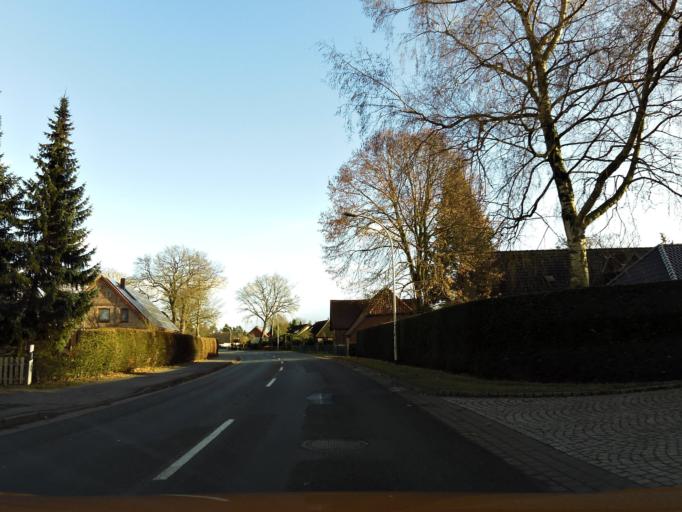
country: DE
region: Lower Saxony
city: Verden
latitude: 52.9073
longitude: 9.2658
